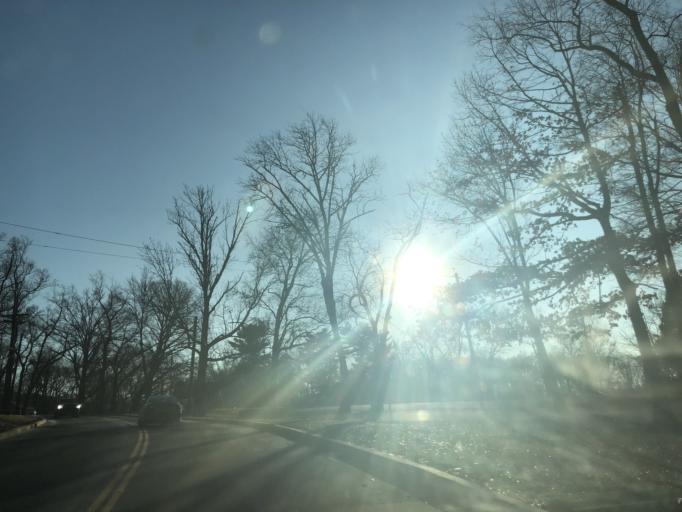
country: US
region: New Jersey
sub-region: Middlesex County
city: Metuchen
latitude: 40.5496
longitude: -74.3401
